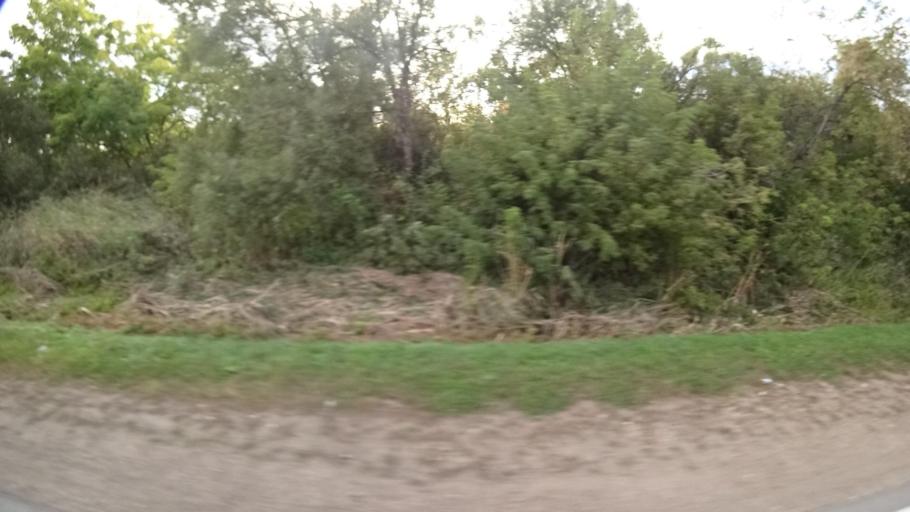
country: RU
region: Primorskiy
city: Dostoyevka
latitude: 44.2884
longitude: 133.4265
